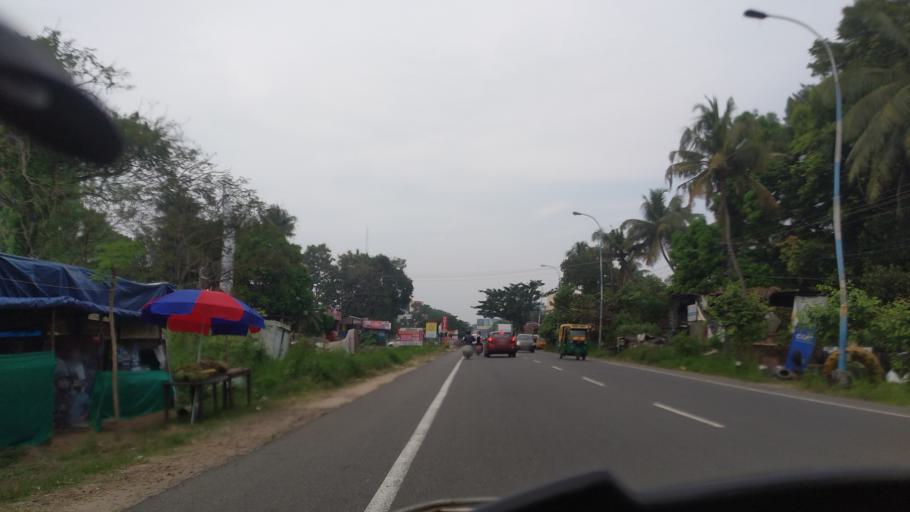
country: IN
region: Kerala
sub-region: Ernakulam
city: Elur
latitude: 10.0462
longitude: 76.2970
